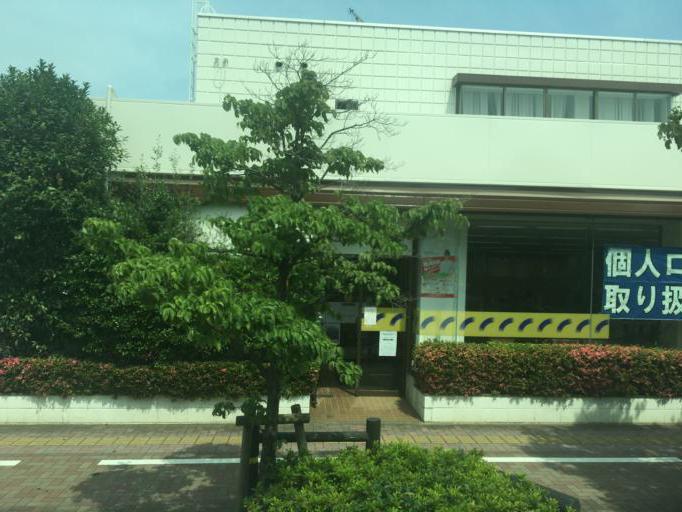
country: JP
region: Tokyo
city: Tanashicho
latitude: 35.7553
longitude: 139.5480
